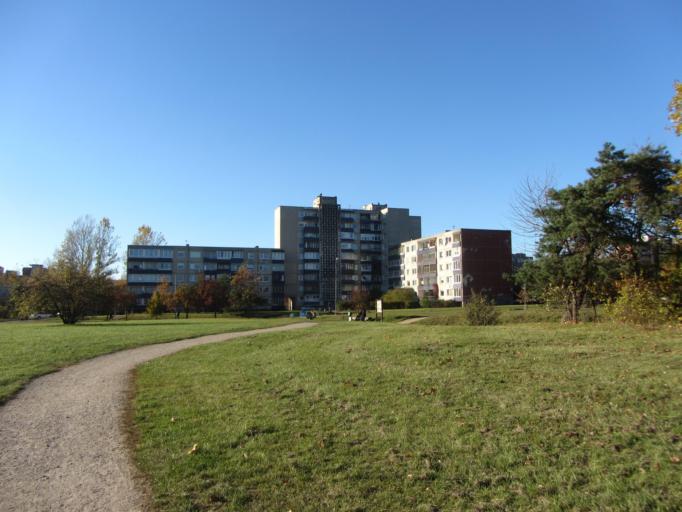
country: LT
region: Vilnius County
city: Justiniskes
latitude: 54.6950
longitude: 25.2286
